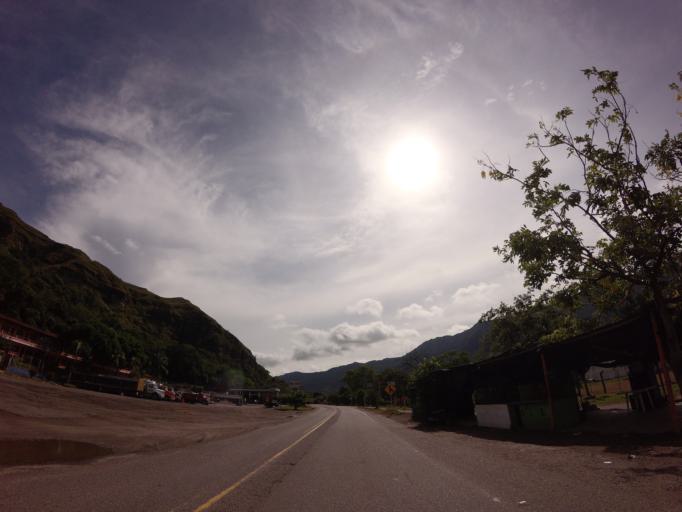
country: CO
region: Tolima
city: Honda
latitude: 5.2291
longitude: -74.7340
